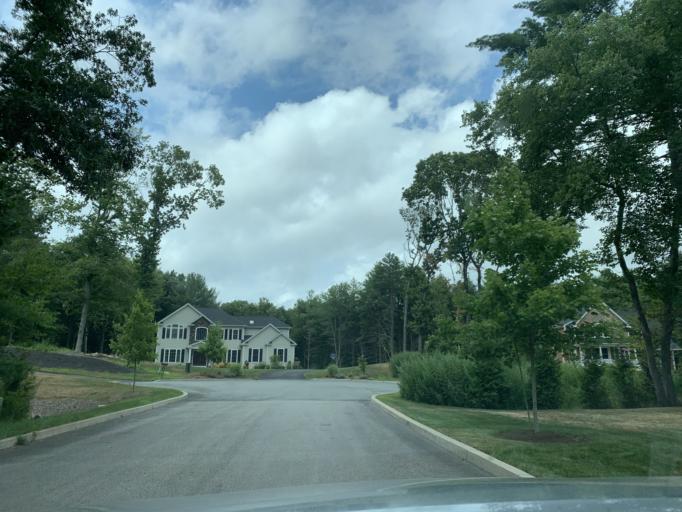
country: US
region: Rhode Island
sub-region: Kent County
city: West Warwick
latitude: 41.6544
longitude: -71.5271
